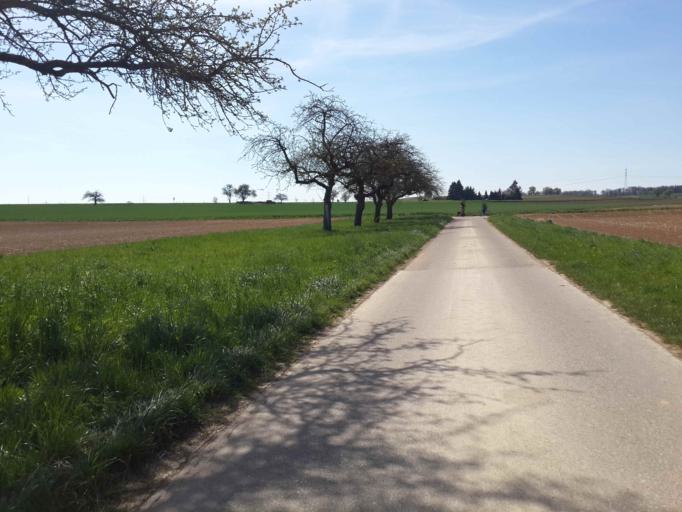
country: DE
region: Baden-Wuerttemberg
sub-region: Regierungsbezirk Stuttgart
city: Leingarten
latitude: 49.1695
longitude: 9.1632
